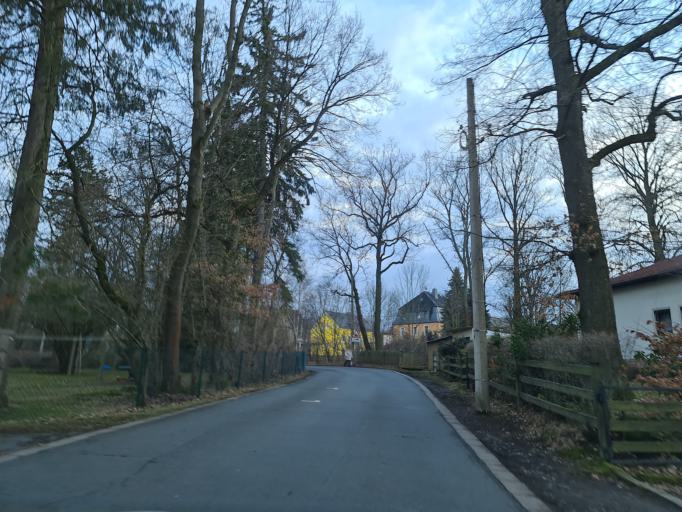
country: DE
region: Saxony
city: Lichtenstein
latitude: 50.7492
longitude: 12.6318
